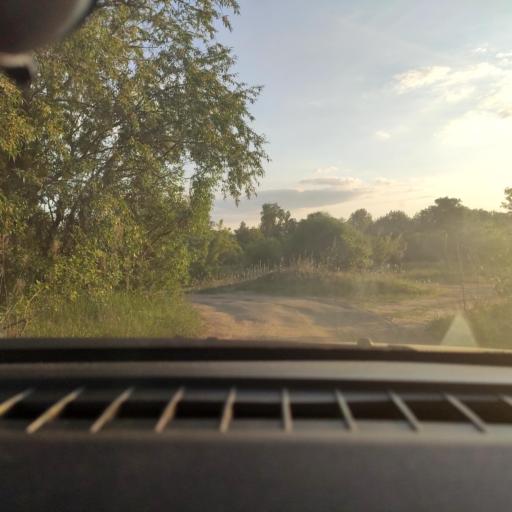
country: RU
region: Voronezj
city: Shilovo
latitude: 51.5363
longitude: 39.1294
